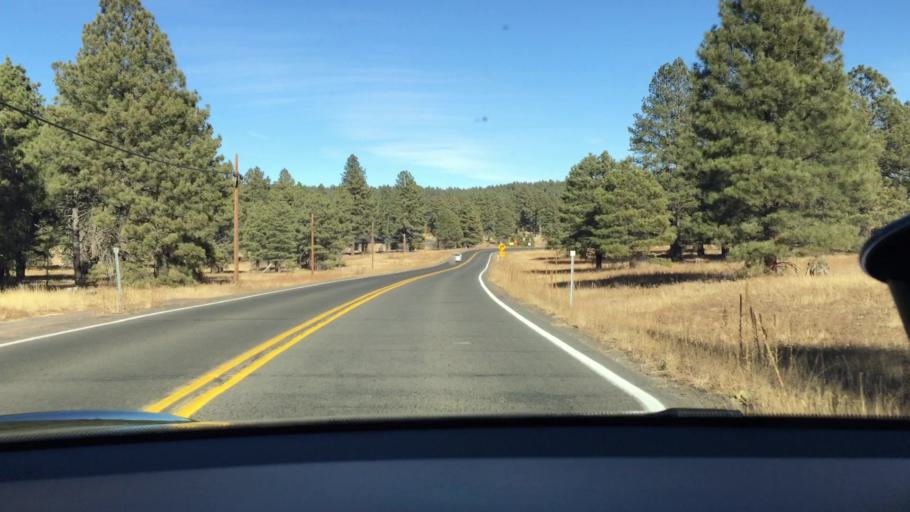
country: US
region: Arizona
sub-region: Coconino County
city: Kachina Village
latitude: 35.0916
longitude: -111.6812
